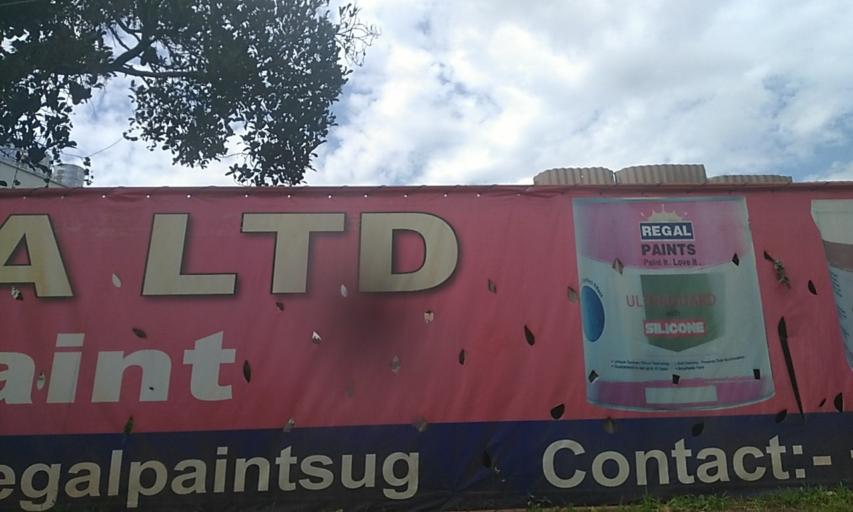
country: UG
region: Central Region
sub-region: Kampala District
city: Kampala
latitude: 0.3286
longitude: 32.6031
